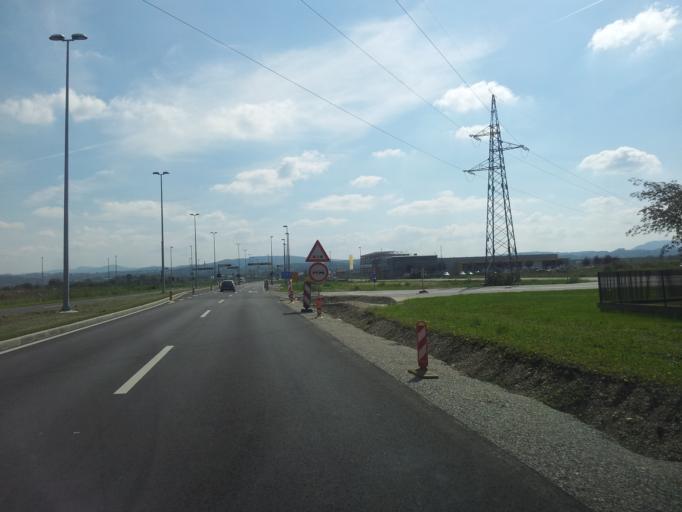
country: HR
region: Varazdinska
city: Varazdin
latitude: 46.2749
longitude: 16.3611
